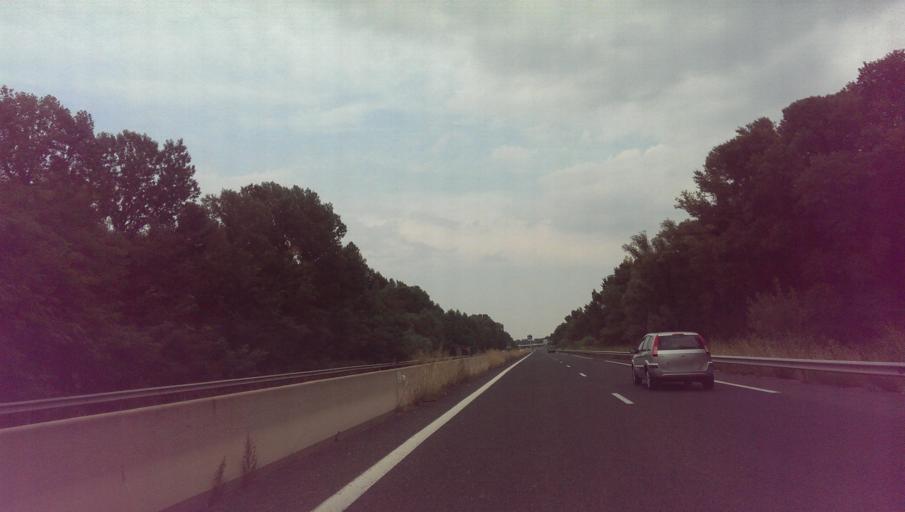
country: FR
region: Languedoc-Roussillon
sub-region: Departement des Pyrenees-Orientales
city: Corneilla-la-Riviere
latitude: 42.6855
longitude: 2.7390
